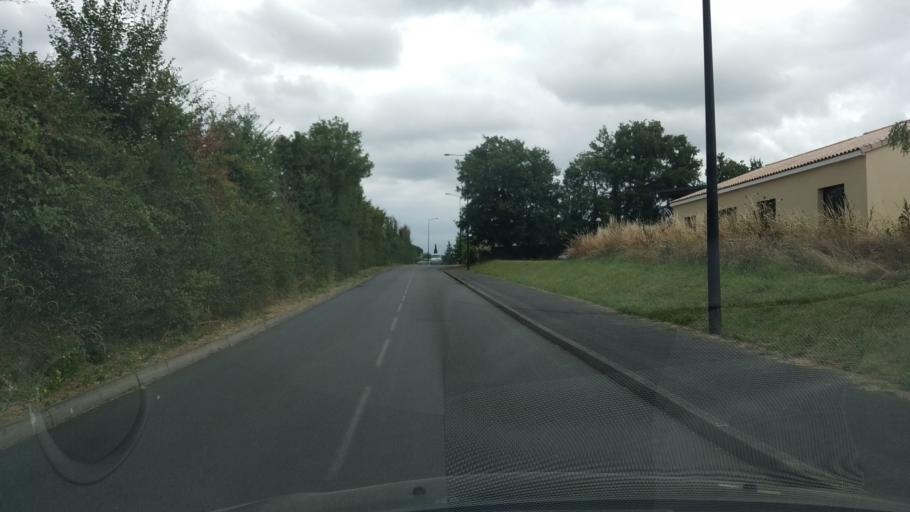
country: FR
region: Poitou-Charentes
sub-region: Departement de la Vienne
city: Smarves
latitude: 46.5092
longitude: 0.3555
